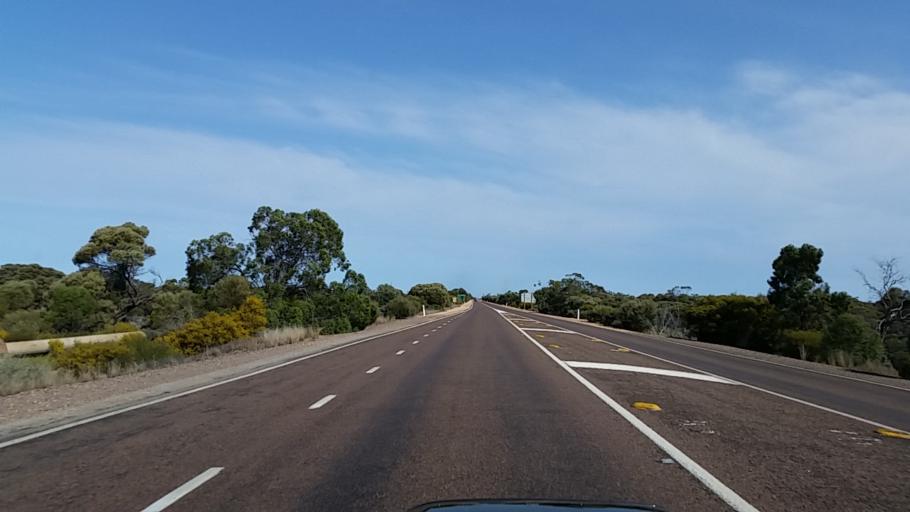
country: AU
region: South Australia
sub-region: Whyalla
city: Whyalla
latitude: -32.9394
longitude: 137.5719
